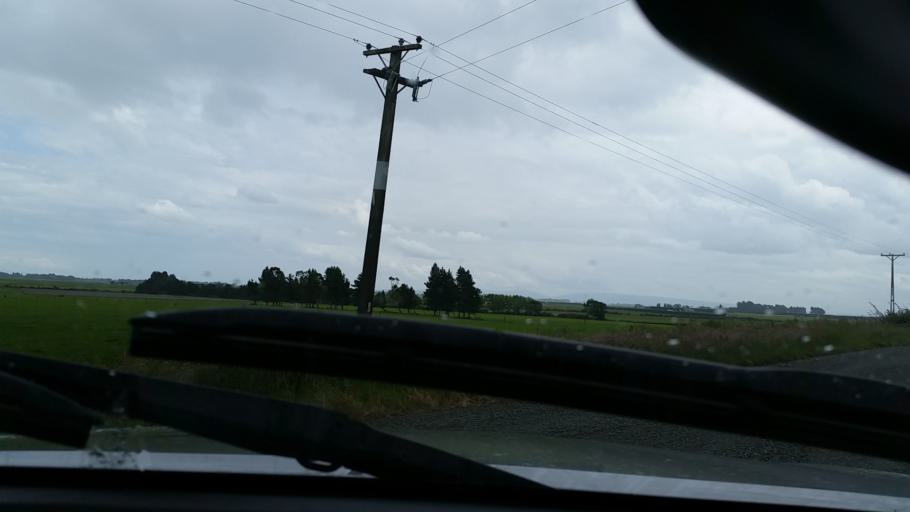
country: NZ
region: Southland
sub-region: Southland District
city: Winton
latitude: -46.0065
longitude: 168.2454
